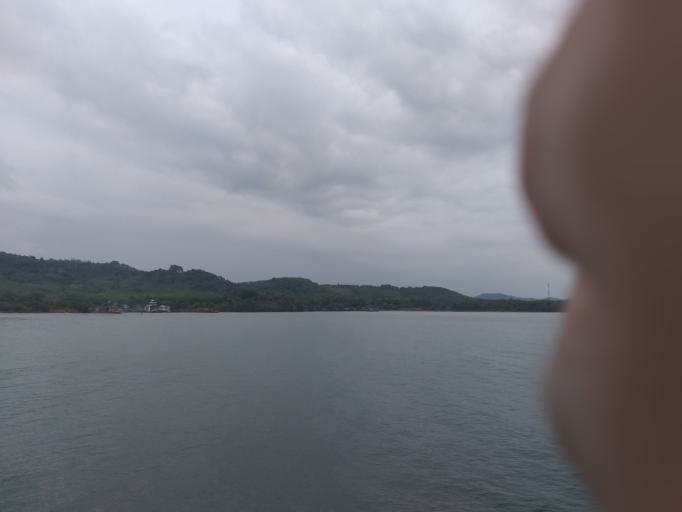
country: TH
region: Trat
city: Laem Ngop
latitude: 12.1793
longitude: 102.3010
